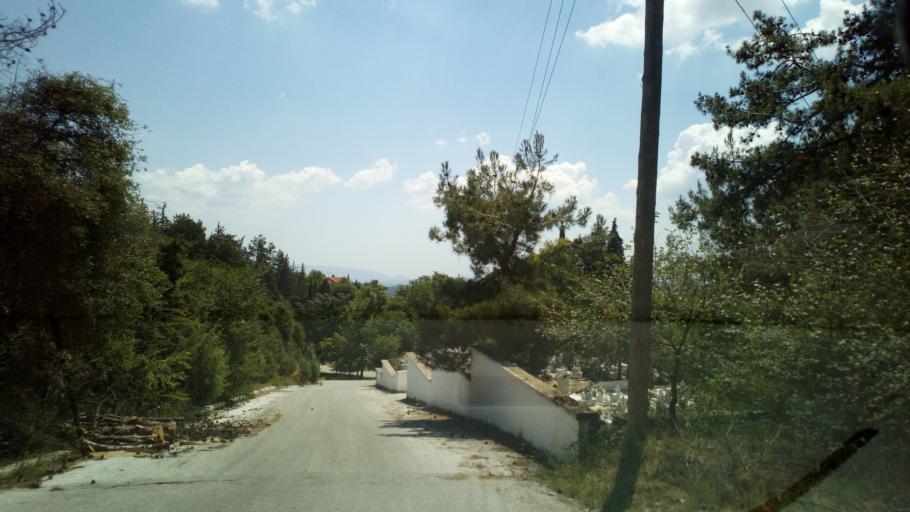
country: GR
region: Central Macedonia
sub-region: Nomos Thessalonikis
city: Sochos
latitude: 40.8206
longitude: 23.3510
